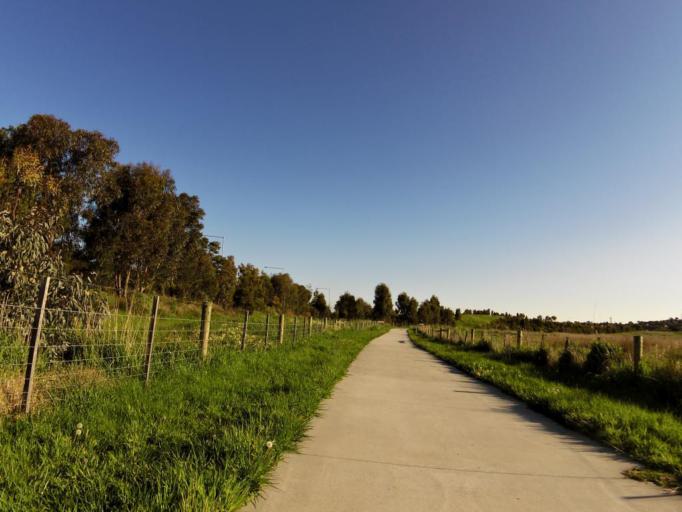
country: AU
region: Victoria
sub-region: Monash
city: Mulgrave
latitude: -37.9214
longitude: 145.2139
